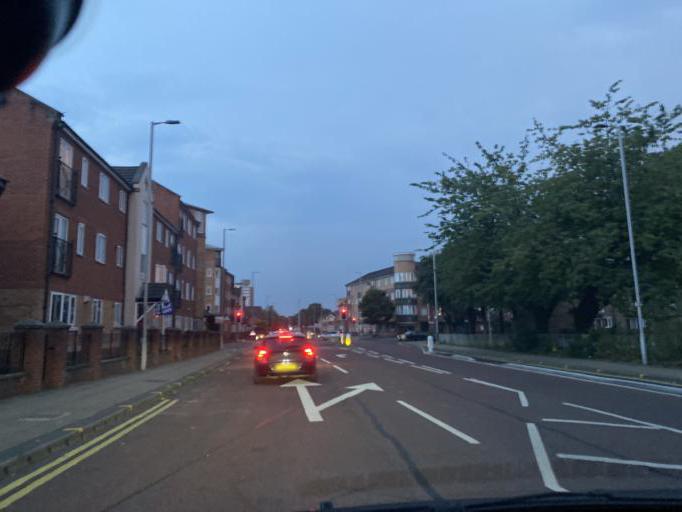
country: GB
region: England
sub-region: Manchester
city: Hulme
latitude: 53.4664
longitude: -2.2577
